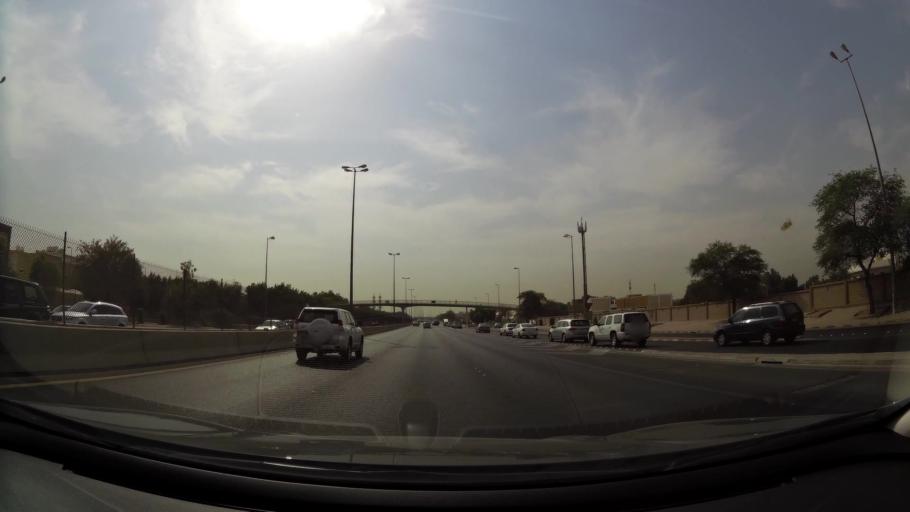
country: KW
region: Al Asimah
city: Ash Shamiyah
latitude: 29.3289
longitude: 47.9719
